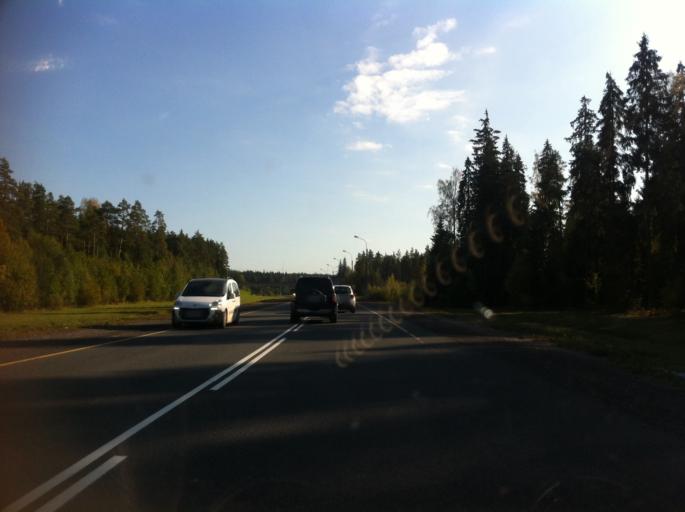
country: RU
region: Leningrad
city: Luga
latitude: 58.7608
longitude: 29.8846
